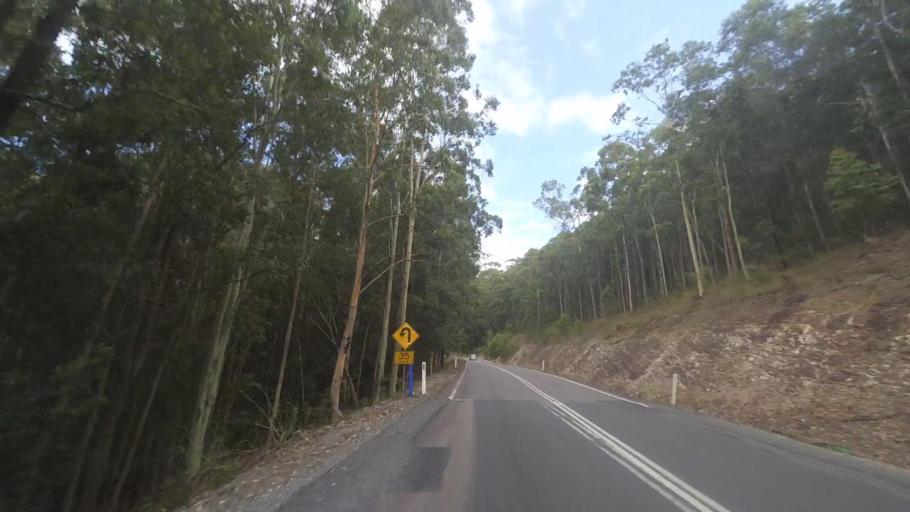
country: AU
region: New South Wales
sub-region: Great Lakes
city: Bulahdelah
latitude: -32.3933
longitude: 152.2447
